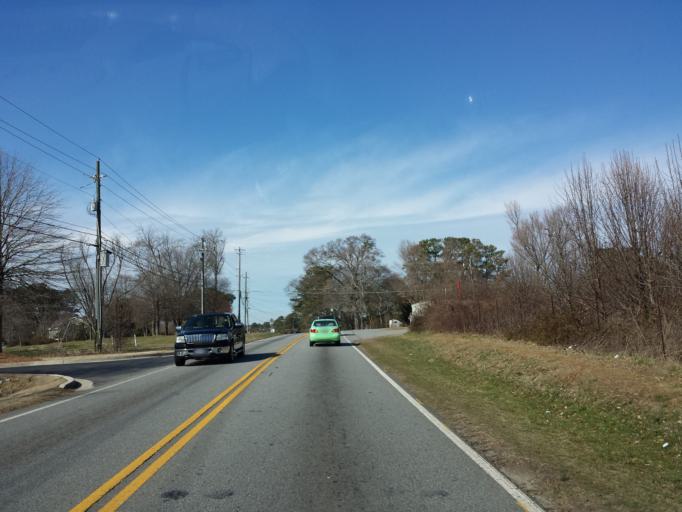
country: US
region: Georgia
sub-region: Cobb County
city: Kennesaw
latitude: 33.9976
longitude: -84.5992
